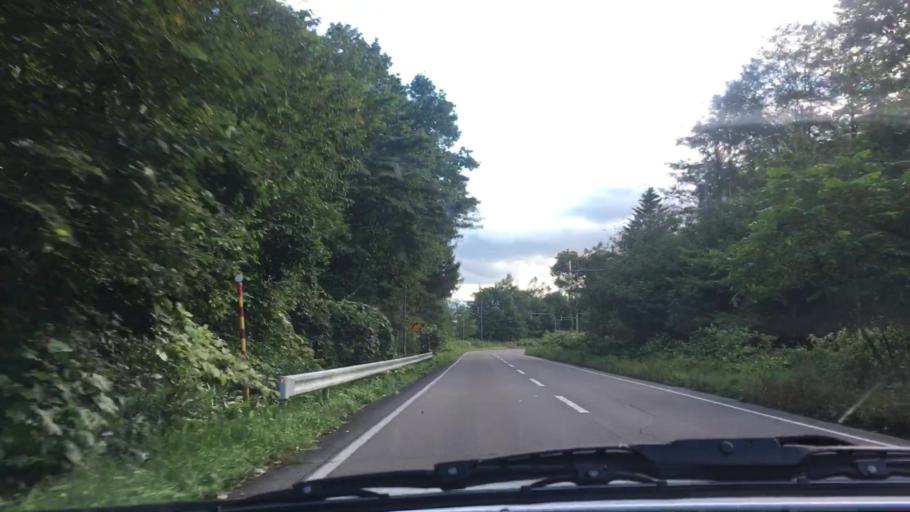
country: JP
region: Hokkaido
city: Otofuke
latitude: 43.1749
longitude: 142.9193
